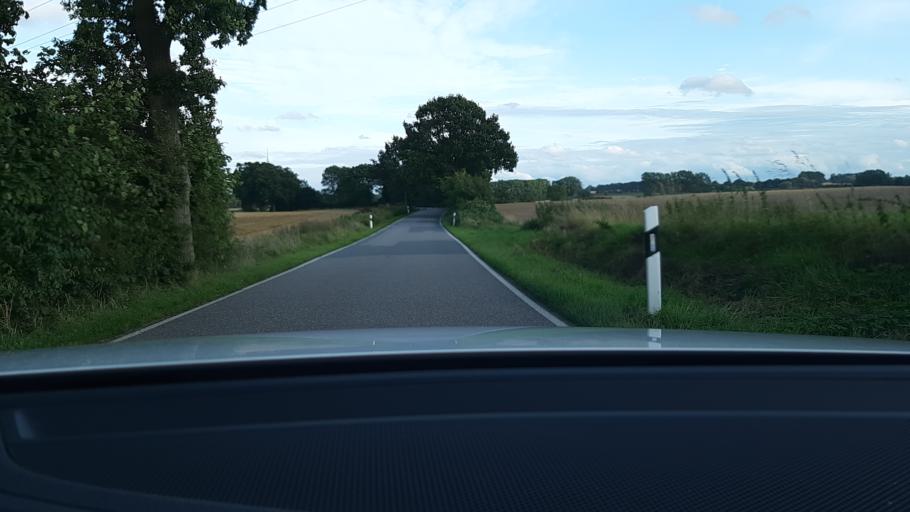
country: DE
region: Schleswig-Holstein
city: Stockelsdorf
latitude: 53.9206
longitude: 10.6186
